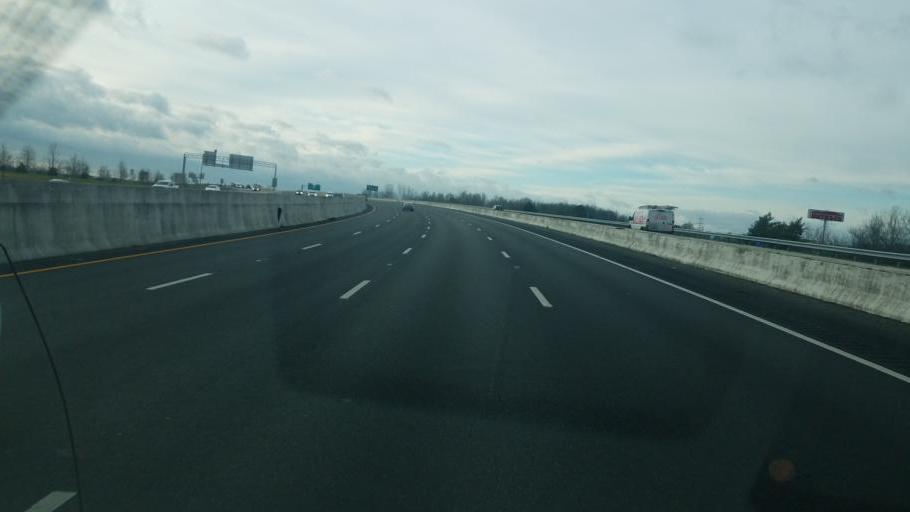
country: US
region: South Carolina
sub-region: York County
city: India Hook
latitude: 34.9794
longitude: -80.9885
